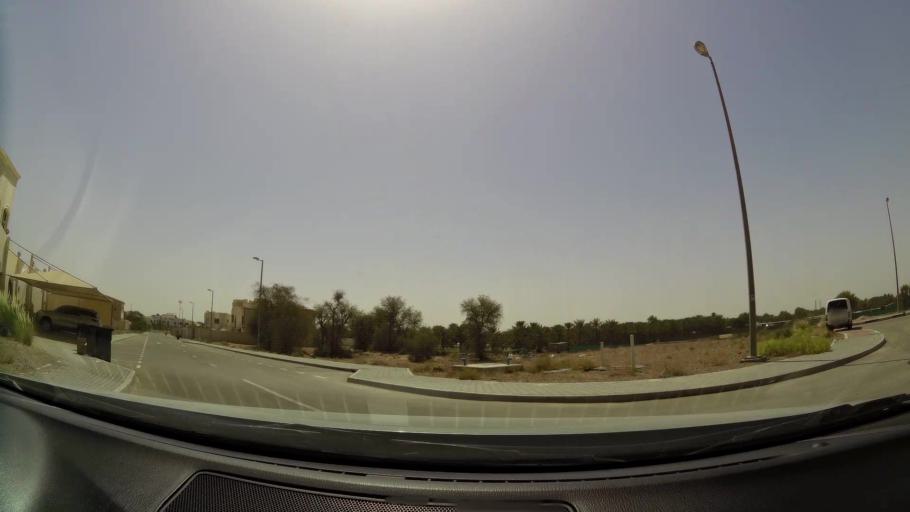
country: OM
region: Al Buraimi
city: Al Buraymi
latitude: 24.2997
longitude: 55.7623
